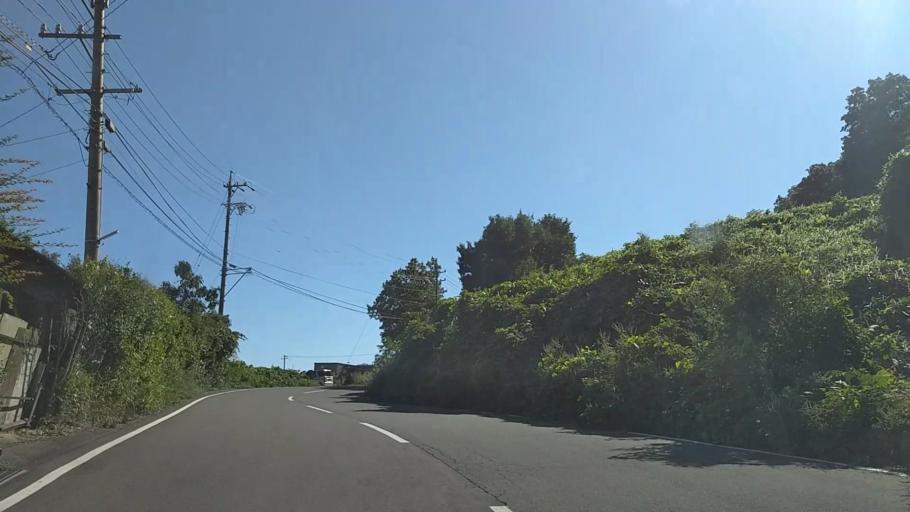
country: JP
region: Nagano
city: Nagano-shi
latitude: 36.5803
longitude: 138.1203
